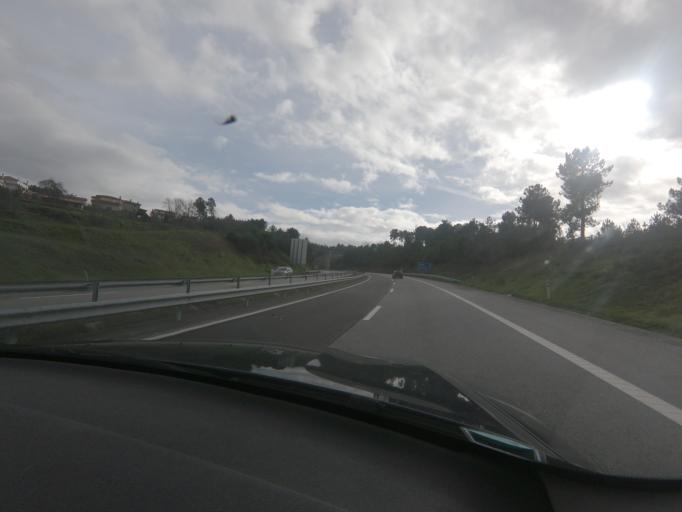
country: PT
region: Vila Real
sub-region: Vila Real
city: Vila Real
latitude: 41.3168
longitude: -7.6953
